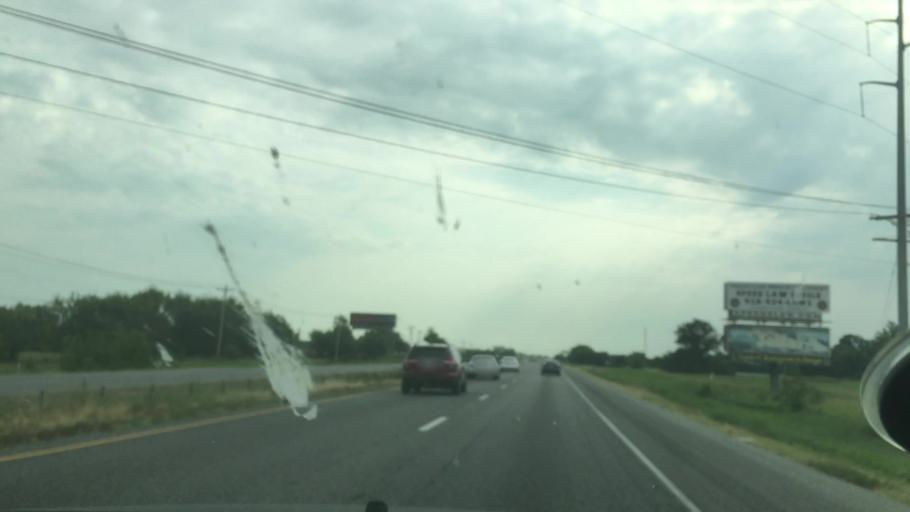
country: US
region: Oklahoma
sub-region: Bryan County
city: Colbert
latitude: 33.8819
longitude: -96.4949
